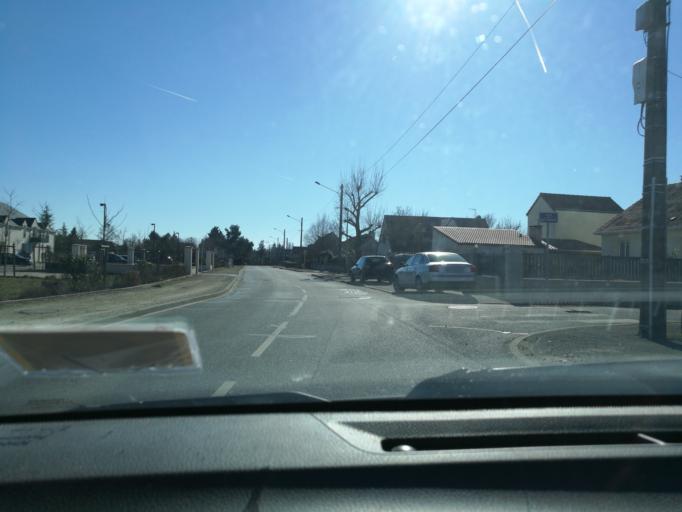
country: FR
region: Centre
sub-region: Departement du Loiret
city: Saint-Jean-le-Blanc
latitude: 47.8807
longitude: 1.9186
